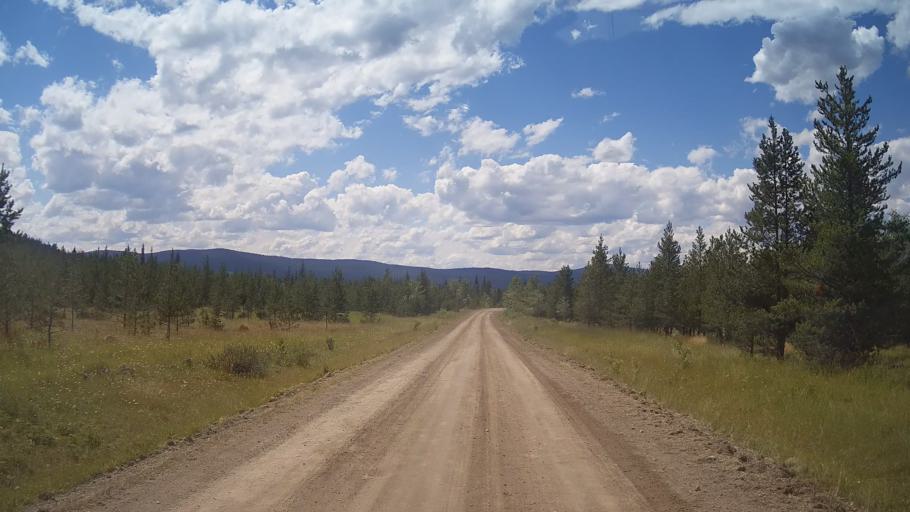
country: CA
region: British Columbia
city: Lillooet
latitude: 51.3401
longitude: -121.9397
